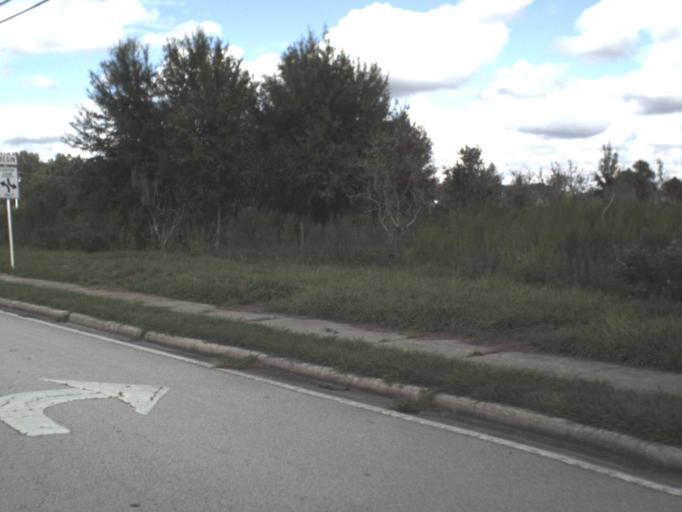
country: US
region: Florida
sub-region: Manatee County
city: Ellenton
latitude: 27.5851
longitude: -82.4255
